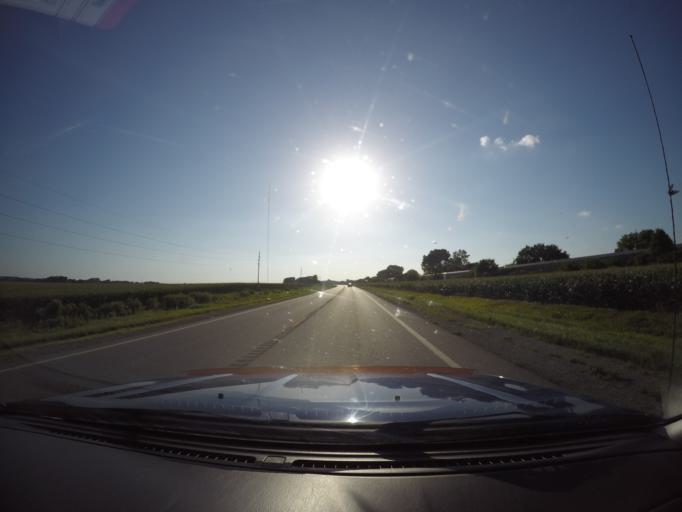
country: US
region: Kansas
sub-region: Shawnee County
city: Silver Lake
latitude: 39.0931
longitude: -95.7736
